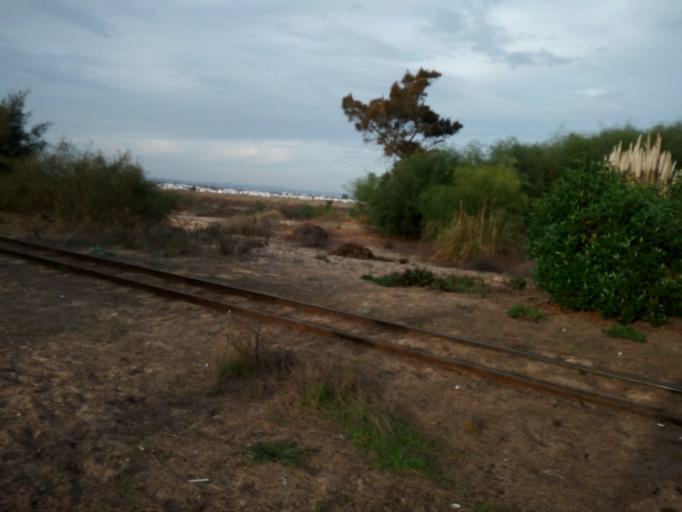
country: PT
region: Faro
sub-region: Tavira
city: Luz
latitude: 37.0877
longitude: -7.6639
